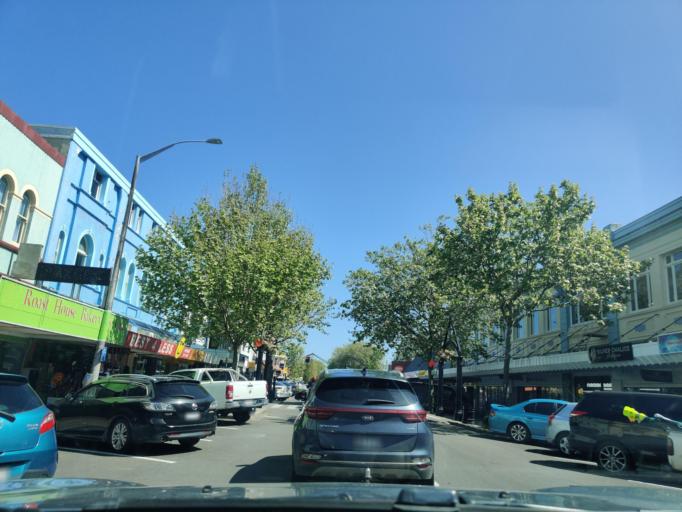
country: NZ
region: Manawatu-Wanganui
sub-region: Wanganui District
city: Wanganui
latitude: -39.9310
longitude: 175.0489
